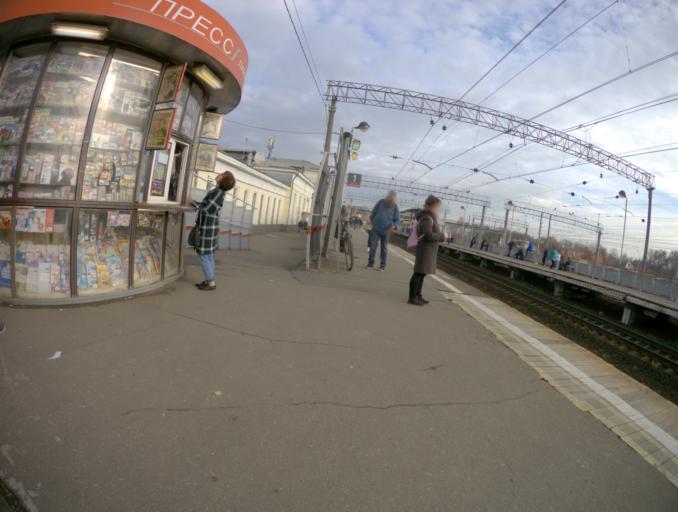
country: RU
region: Moskovskaya
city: Orekhovo-Zuyevo
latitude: 55.7949
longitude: 38.9752
